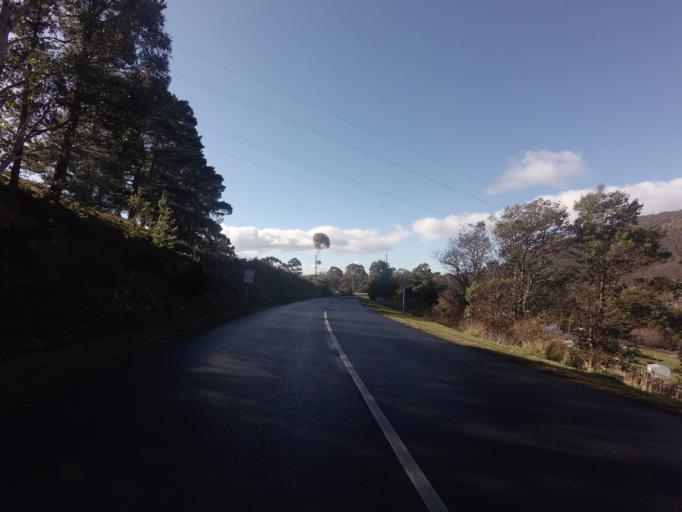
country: AU
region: Tasmania
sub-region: Glenorchy
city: Berriedale
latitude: -42.8251
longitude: 147.2011
